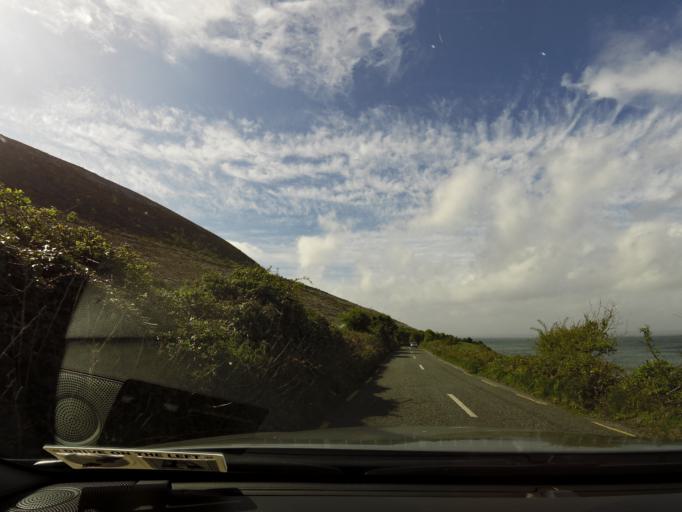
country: IE
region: Connaught
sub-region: County Galway
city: Bearna
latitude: 53.1448
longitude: -9.2347
